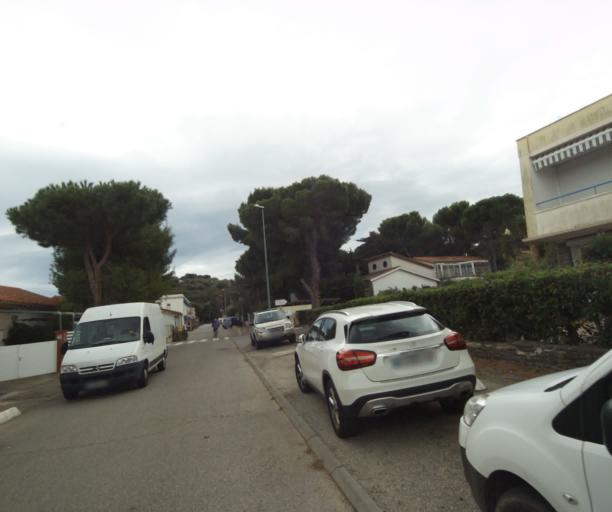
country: FR
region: Languedoc-Roussillon
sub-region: Departement des Pyrenees-Orientales
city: Collioure
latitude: 42.5368
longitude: 3.0553
